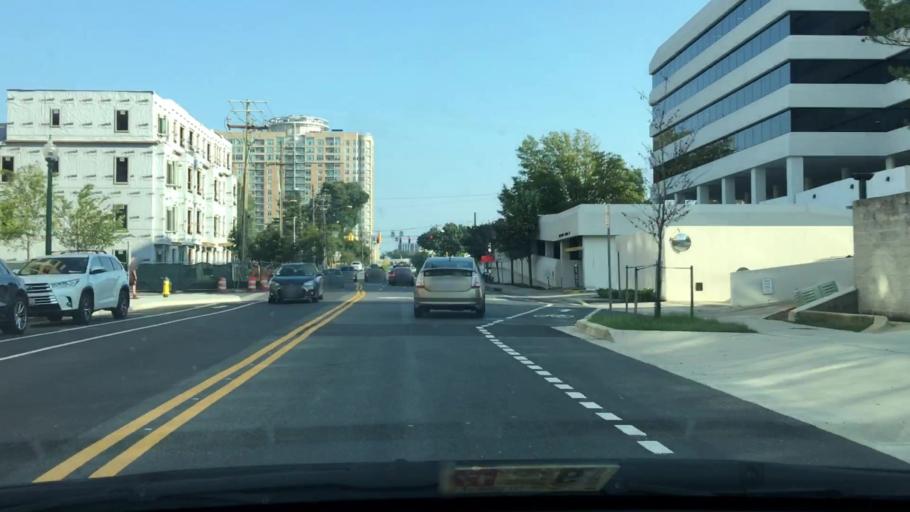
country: US
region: Maryland
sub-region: Montgomery County
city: North Bethesda
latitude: 39.0598
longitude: -77.1199
